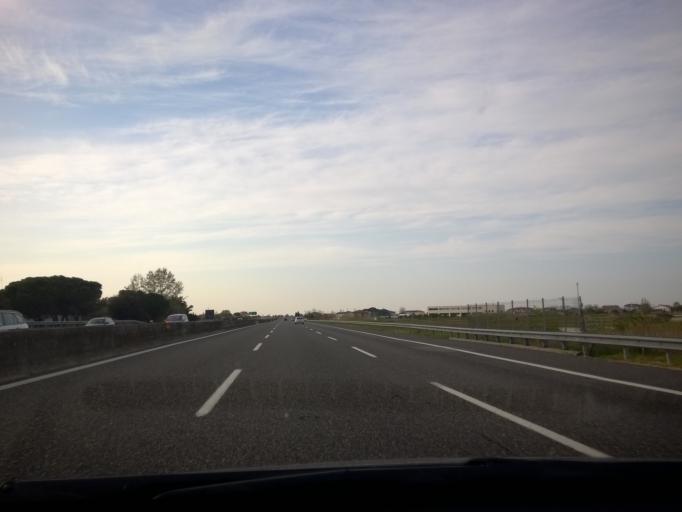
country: IT
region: Emilia-Romagna
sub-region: Forli-Cesena
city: Gatteo-Sant'Angelo
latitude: 44.1250
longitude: 12.3832
